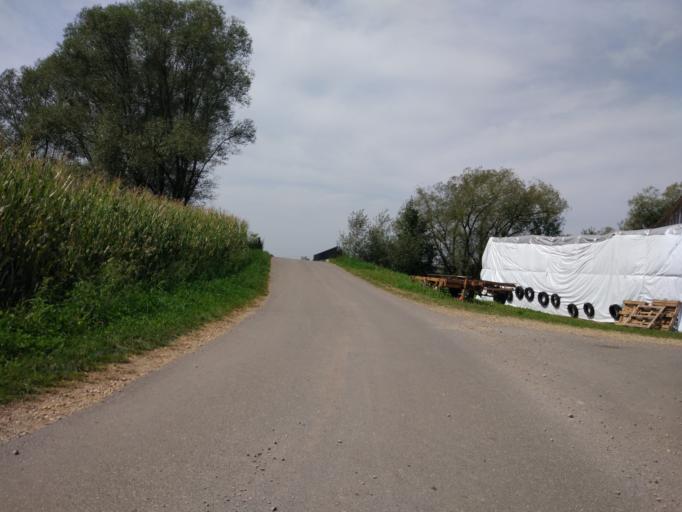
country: DE
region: Baden-Wuerttemberg
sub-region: Tuebingen Region
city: Achstetten
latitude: 48.2837
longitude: 9.8969
